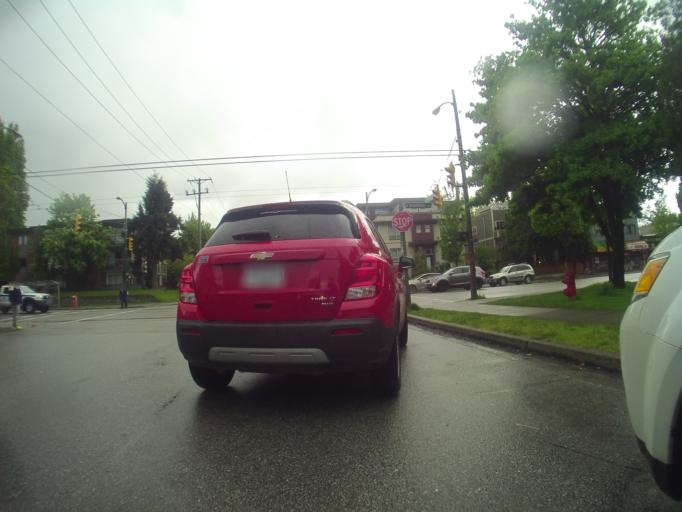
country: CA
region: British Columbia
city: Vancouver
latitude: 49.2627
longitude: -123.0737
